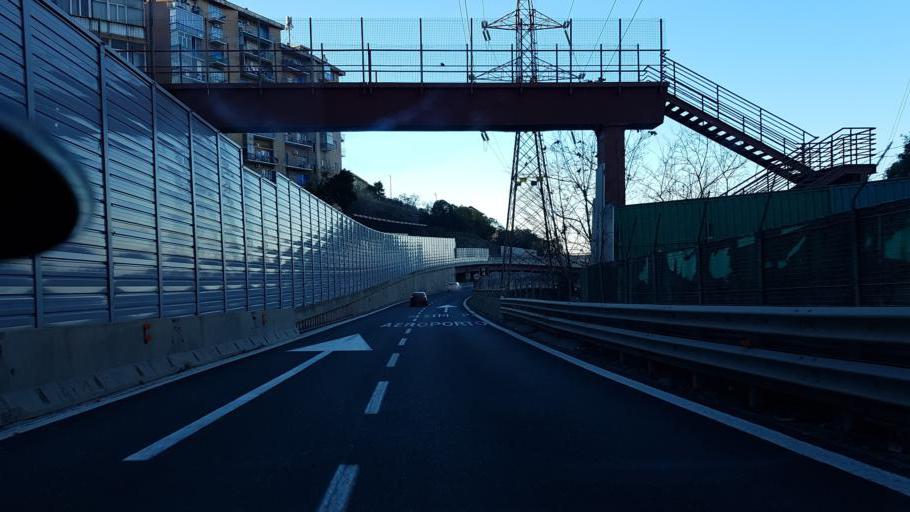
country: IT
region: Liguria
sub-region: Provincia di Genova
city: San Teodoro
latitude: 44.4187
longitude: 8.8660
